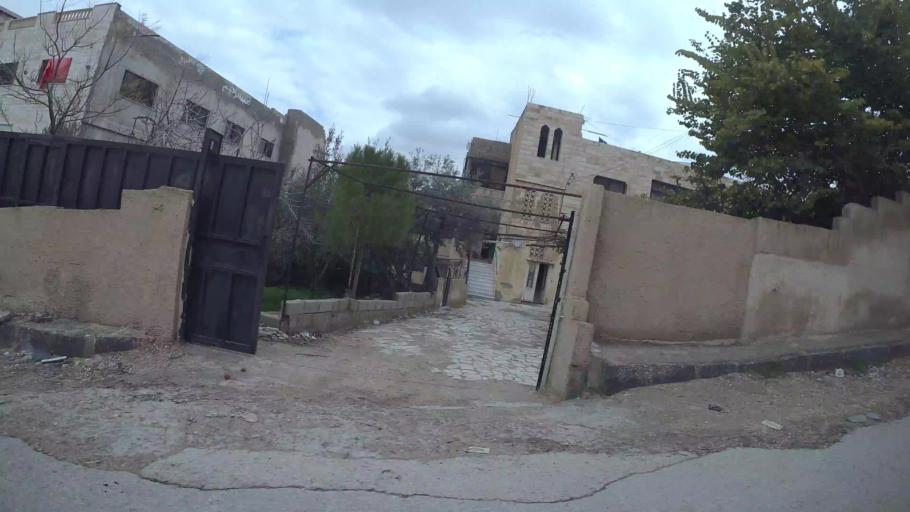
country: JO
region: Amman
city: Al Jubayhah
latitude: 32.0490
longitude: 35.8396
